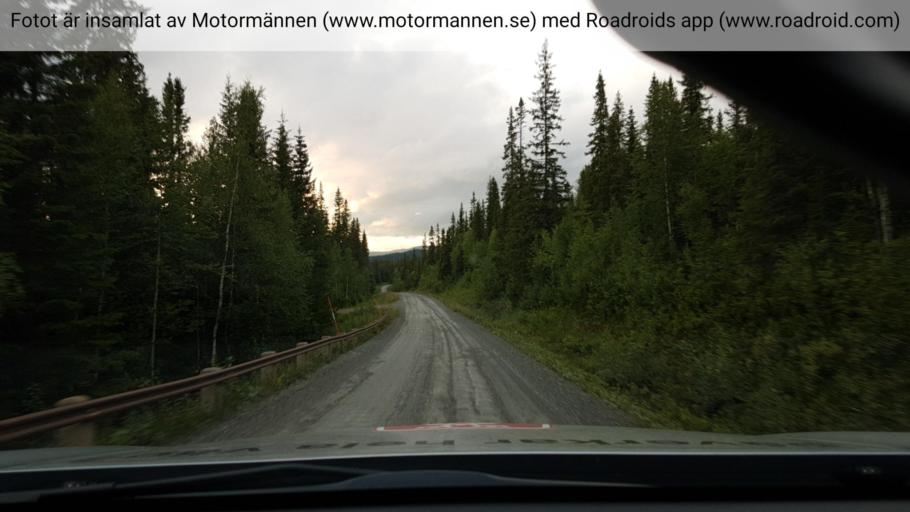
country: SE
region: Vaesterbotten
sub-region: Vilhelmina Kommun
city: Sjoberg
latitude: 65.5013
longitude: 15.4828
